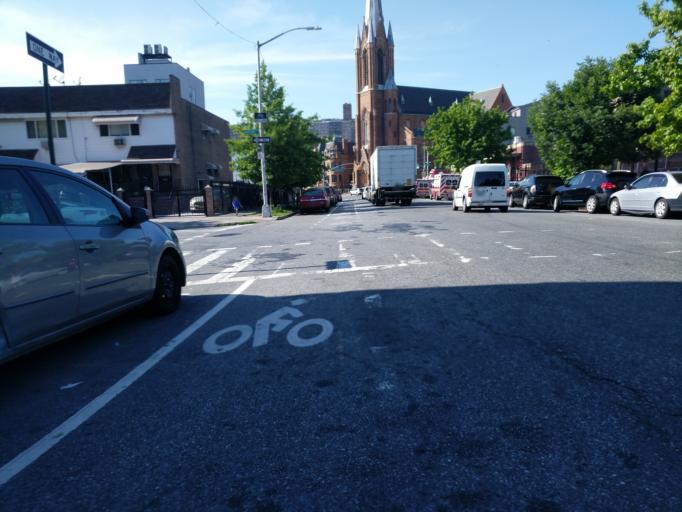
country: US
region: New York
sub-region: Queens County
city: Long Island City
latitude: 40.6996
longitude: -73.9443
